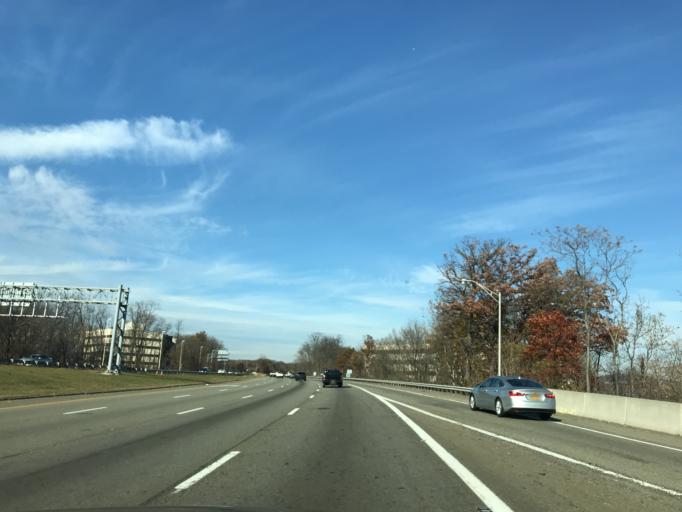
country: US
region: New Jersey
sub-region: Morris County
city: Parsippany
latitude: 40.8666
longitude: -74.4168
